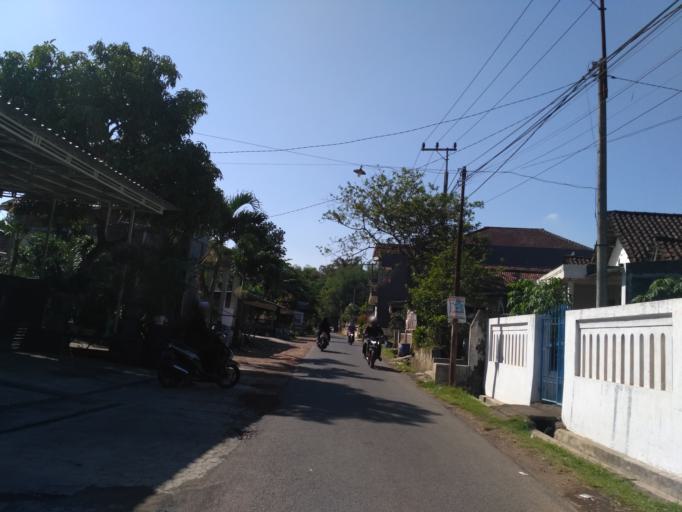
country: ID
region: East Java
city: Singosari
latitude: -7.9173
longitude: 112.6657
